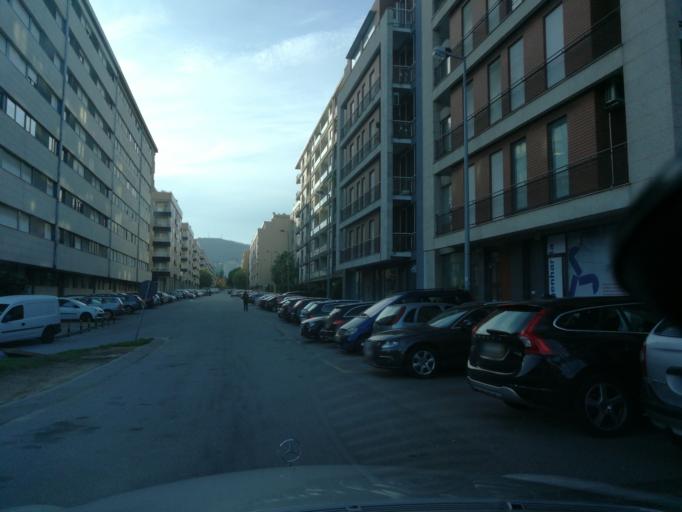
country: PT
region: Braga
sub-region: Braga
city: Braga
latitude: 41.5476
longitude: -8.4059
